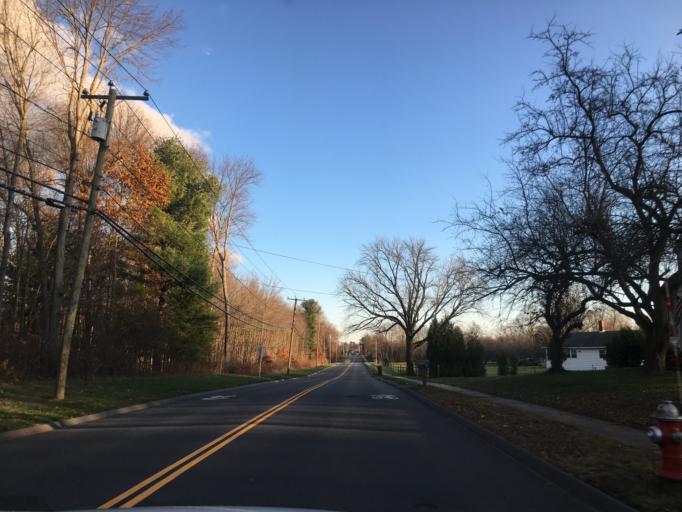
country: US
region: Connecticut
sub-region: Hartford County
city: Enfield
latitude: 41.9681
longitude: -72.5854
